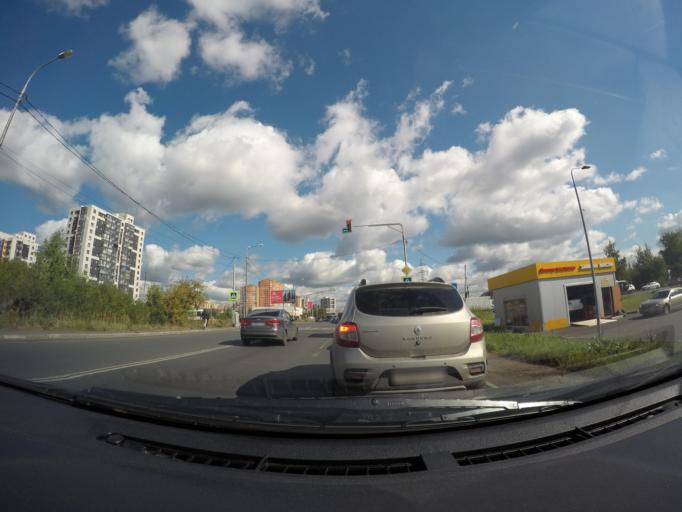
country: RU
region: Moskovskaya
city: Ramenskoye
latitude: 55.5876
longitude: 38.2500
